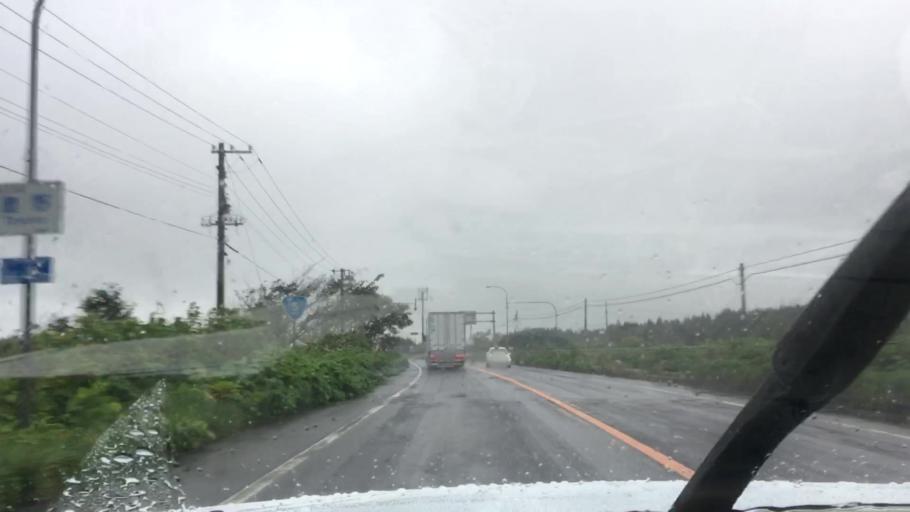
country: JP
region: Hokkaido
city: Niseko Town
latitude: 42.4337
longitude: 140.3197
